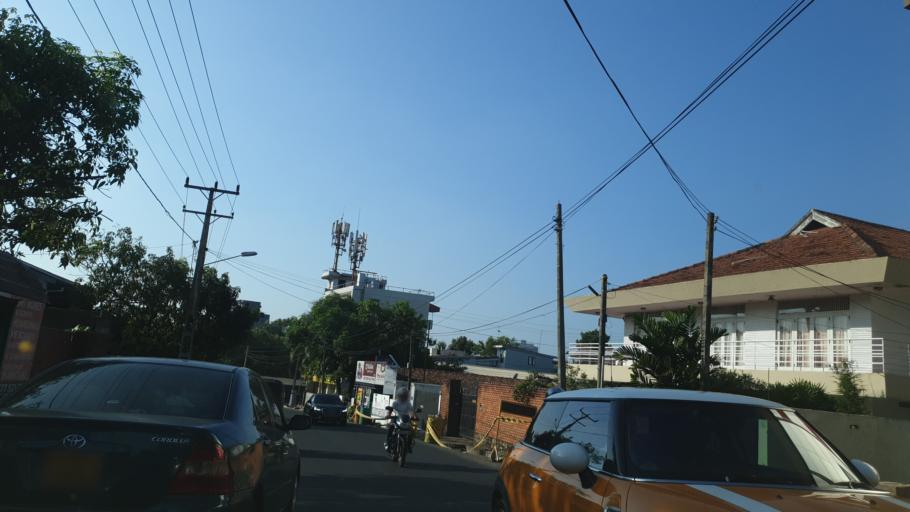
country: LK
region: Western
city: Sri Jayewardenepura Kotte
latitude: 6.8727
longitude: 79.9049
